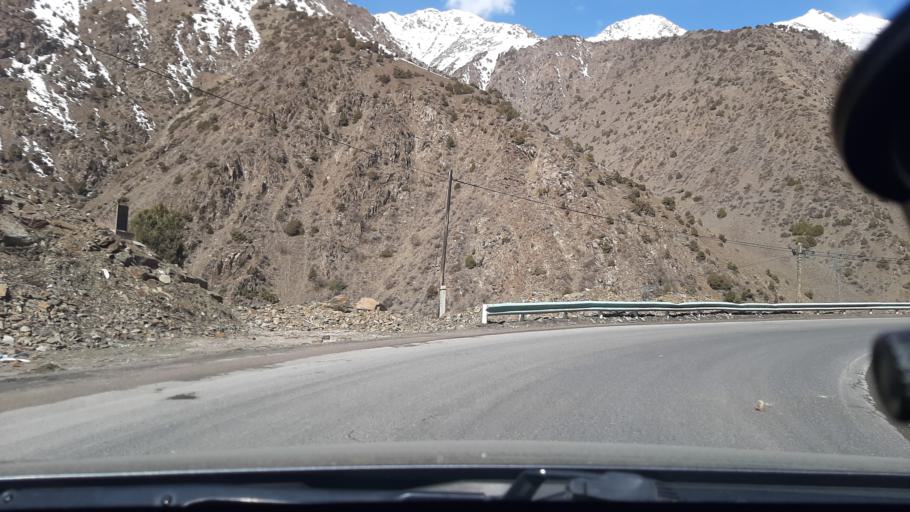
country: TJ
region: Viloyati Sughd
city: Ayni
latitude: 39.5061
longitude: 68.5516
